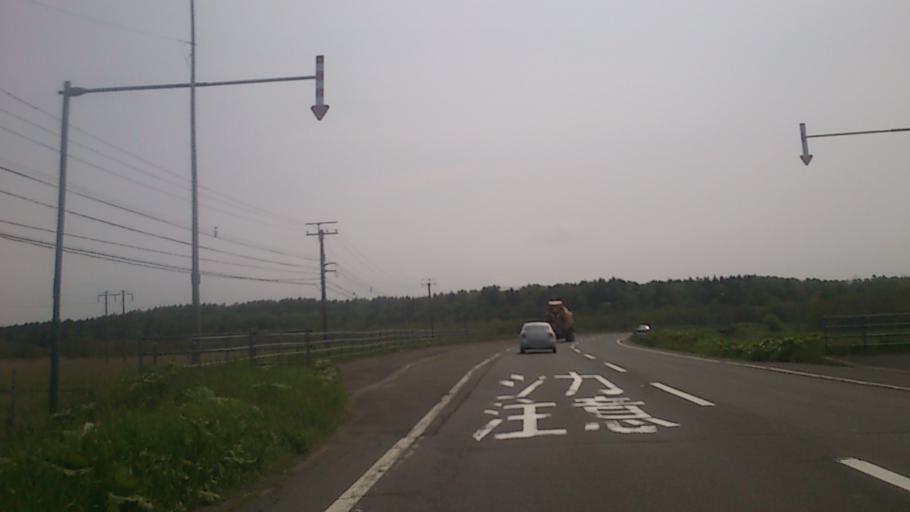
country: JP
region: Hokkaido
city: Nemuro
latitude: 43.2624
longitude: 145.4616
